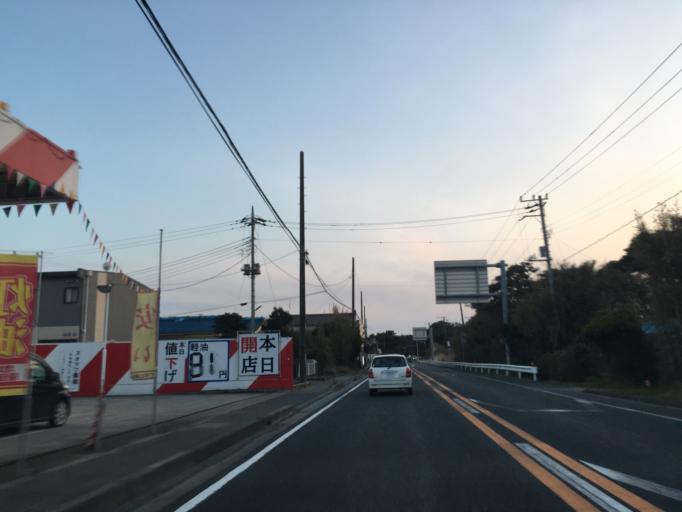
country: JP
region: Ibaraki
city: Kitaibaraki
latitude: 36.7875
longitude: 140.7491
